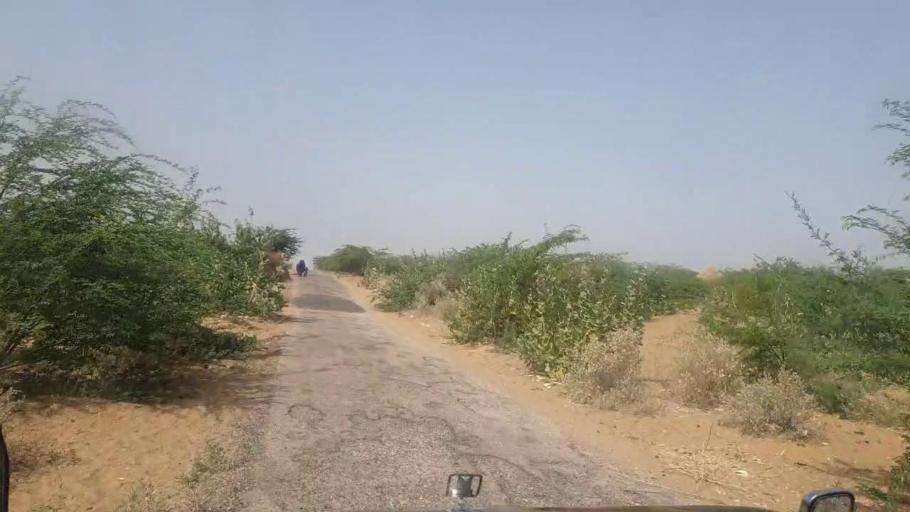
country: PK
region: Sindh
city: Islamkot
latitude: 25.1110
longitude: 70.1975
